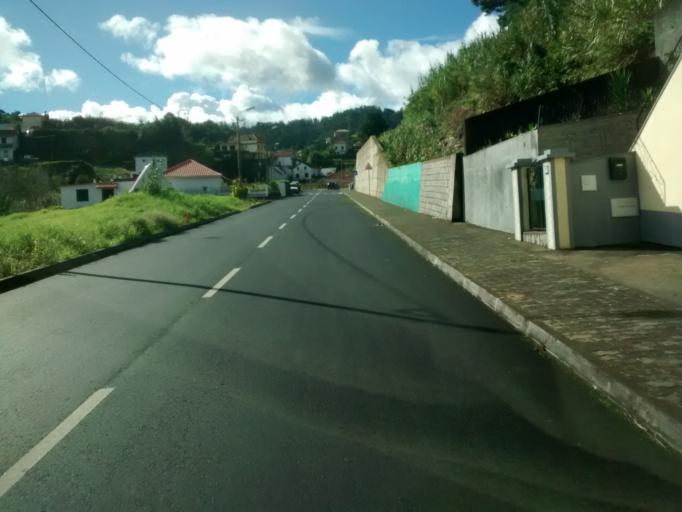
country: PT
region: Madeira
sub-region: Santana
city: Santana
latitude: 32.8067
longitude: -16.8849
